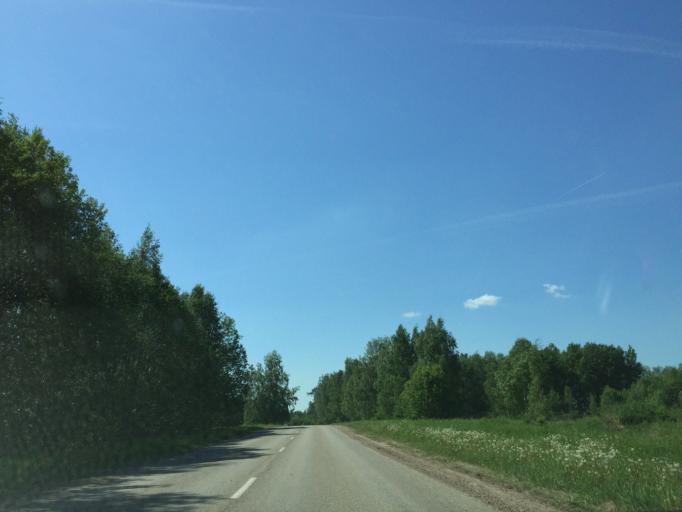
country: LV
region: Bauskas Rajons
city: Bauska
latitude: 56.4262
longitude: 24.2927
